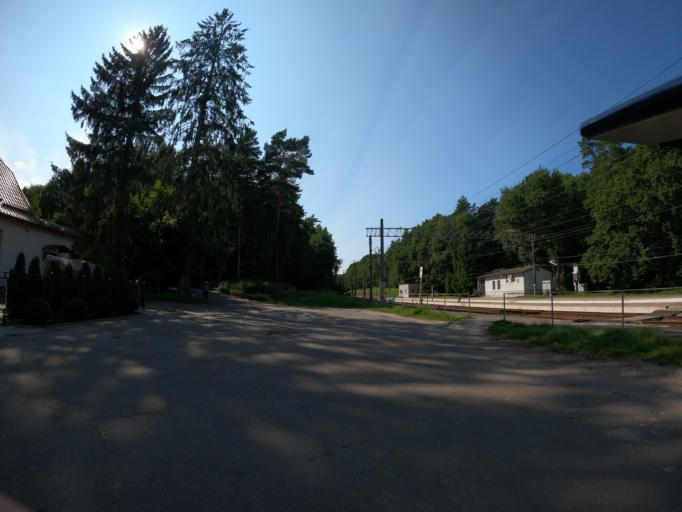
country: RU
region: Kaliningrad
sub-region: Gorod Svetlogorsk
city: Svetlogorsk
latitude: 54.9330
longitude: 20.1593
